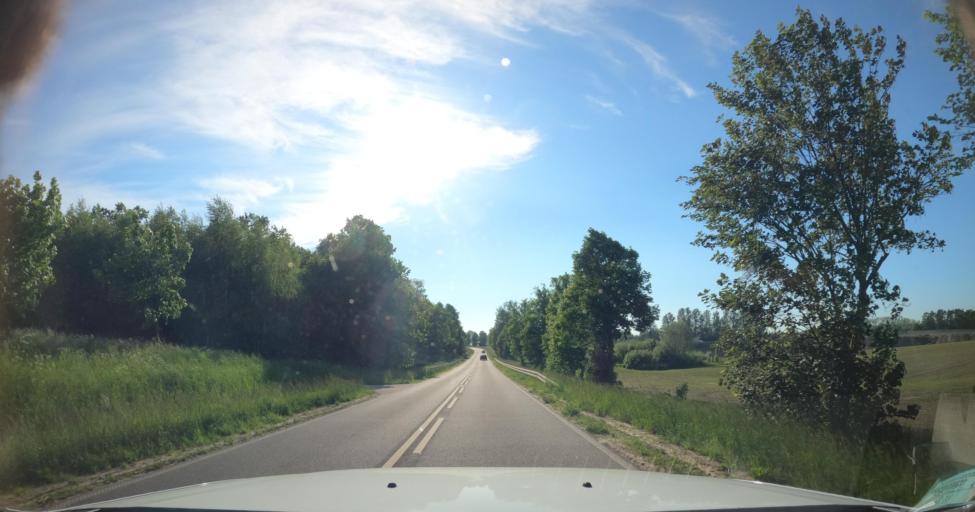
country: PL
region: Warmian-Masurian Voivodeship
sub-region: Powiat elblaski
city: Paslek
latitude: 54.0754
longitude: 19.6837
